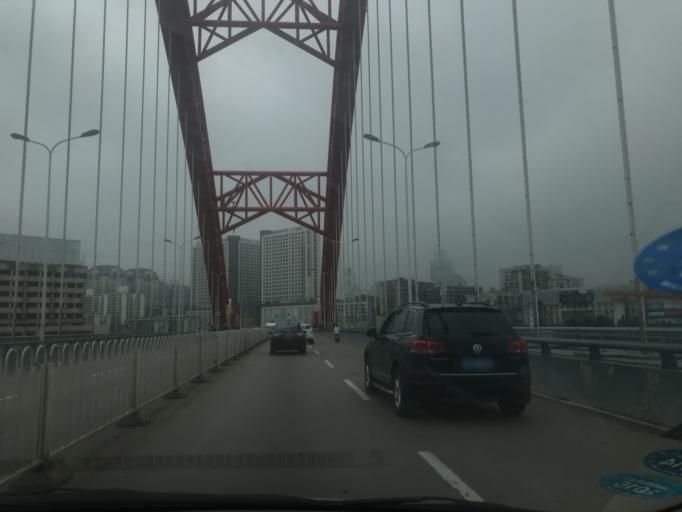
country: CN
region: Hubei
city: Wuhan
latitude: 30.5662
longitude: 114.2788
